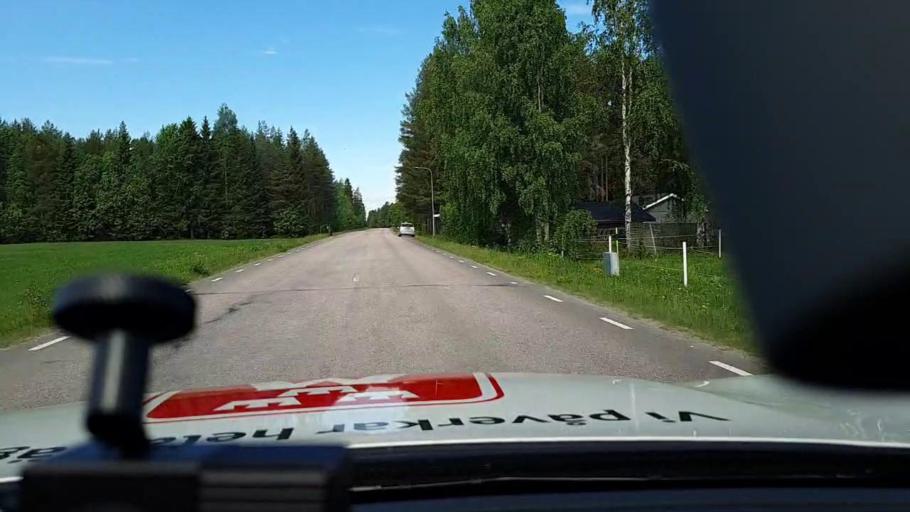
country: SE
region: Norrbotten
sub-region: Lulea Kommun
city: Sodra Sunderbyn
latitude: 65.6453
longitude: 21.8853
